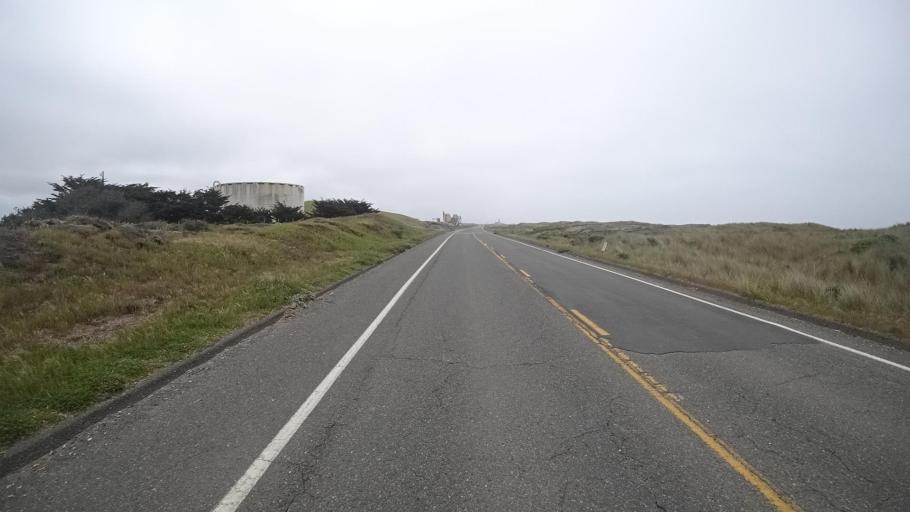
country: US
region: California
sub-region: Humboldt County
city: Eureka
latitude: 40.8061
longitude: -124.1992
